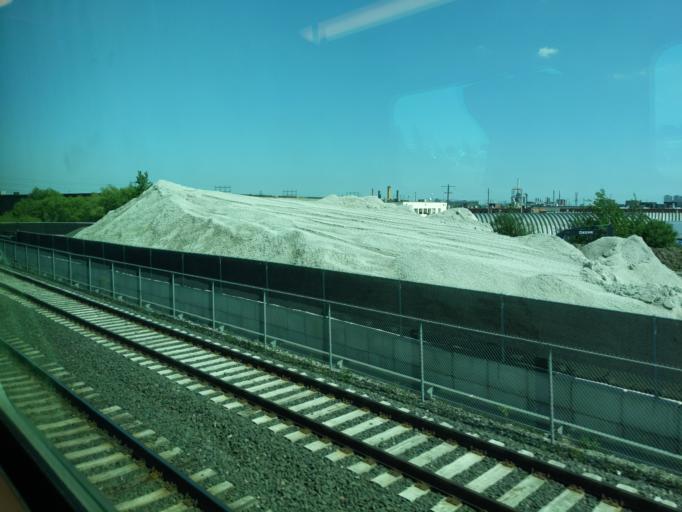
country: CA
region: Ontario
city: Etobicoke
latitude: 43.7056
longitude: -79.5942
